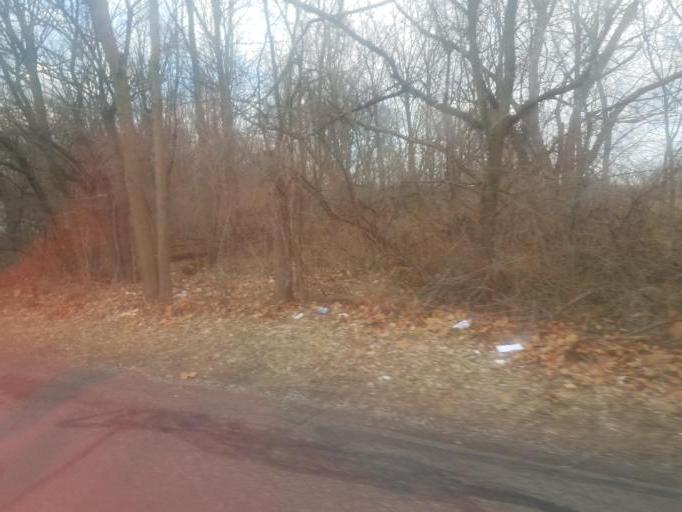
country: US
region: Ohio
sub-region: Marion County
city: Marion
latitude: 40.5767
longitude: -83.1539
